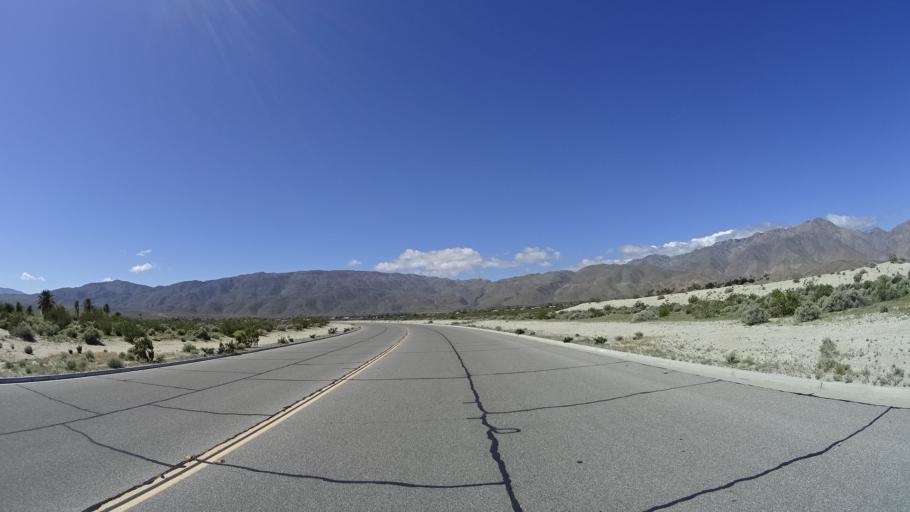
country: US
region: California
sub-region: San Diego County
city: Borrego Springs
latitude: 33.2355
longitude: -116.3592
